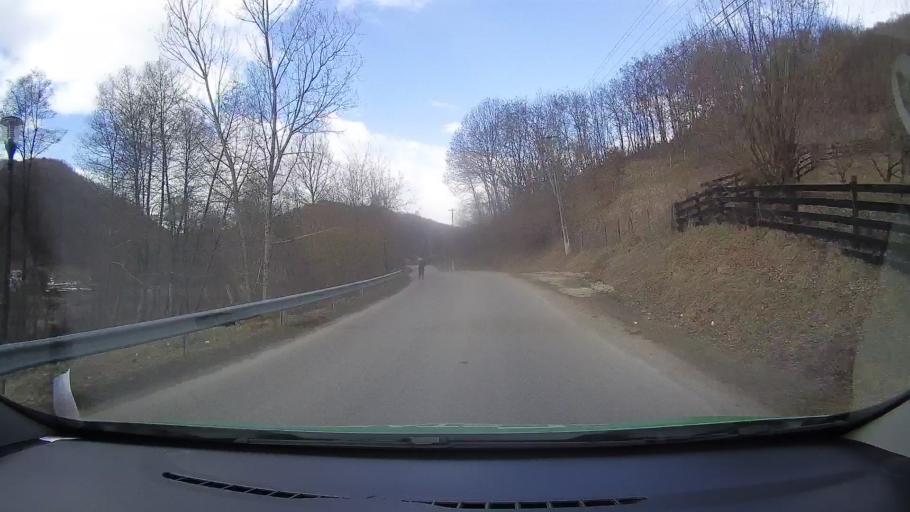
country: RO
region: Dambovita
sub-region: Comuna Varfuri
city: Varfuri
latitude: 45.0790
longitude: 25.5149
